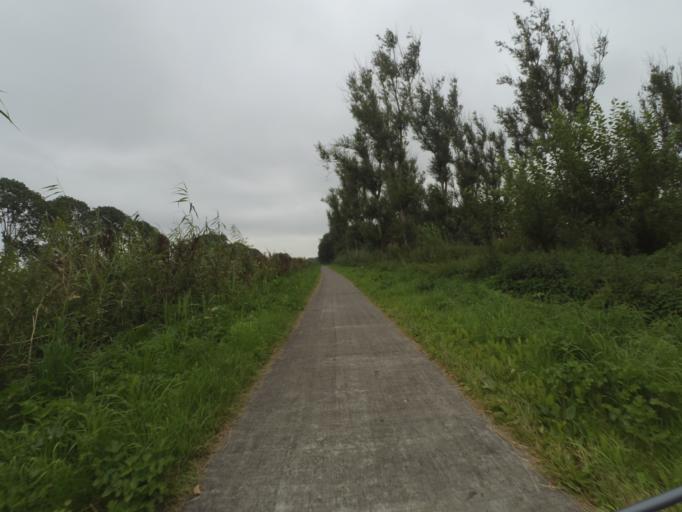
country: NL
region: Flevoland
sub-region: Gemeente Lelystad
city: Lelystad
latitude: 52.4604
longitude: 5.5351
